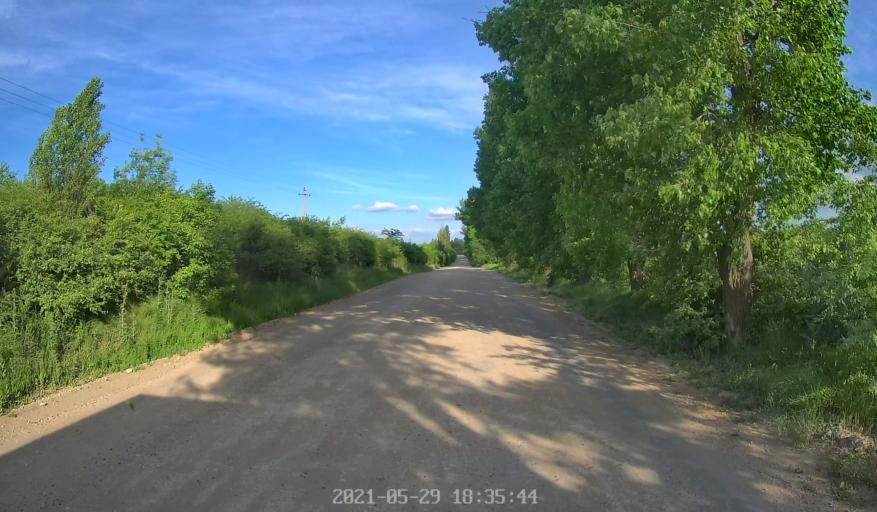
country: MD
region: Chisinau
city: Singera
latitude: 46.8085
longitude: 28.9211
